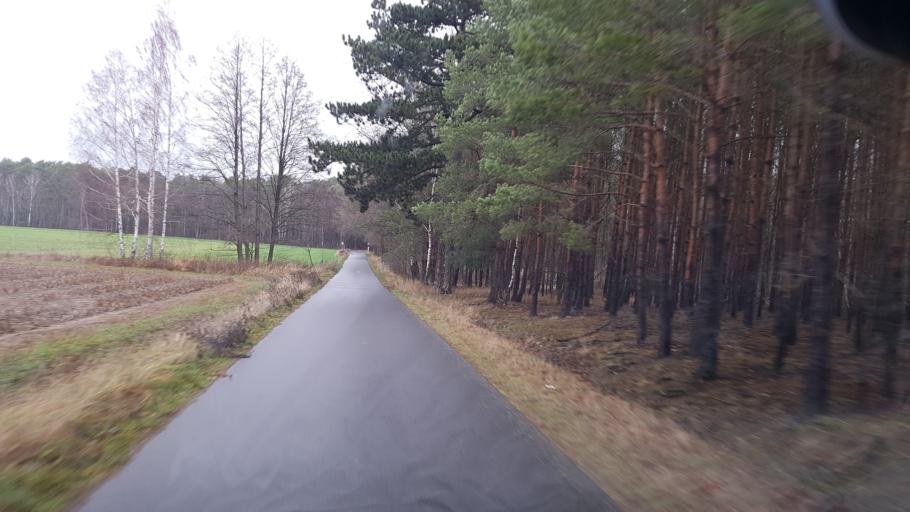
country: DE
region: Brandenburg
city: Altdobern
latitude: 51.6825
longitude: 13.9988
